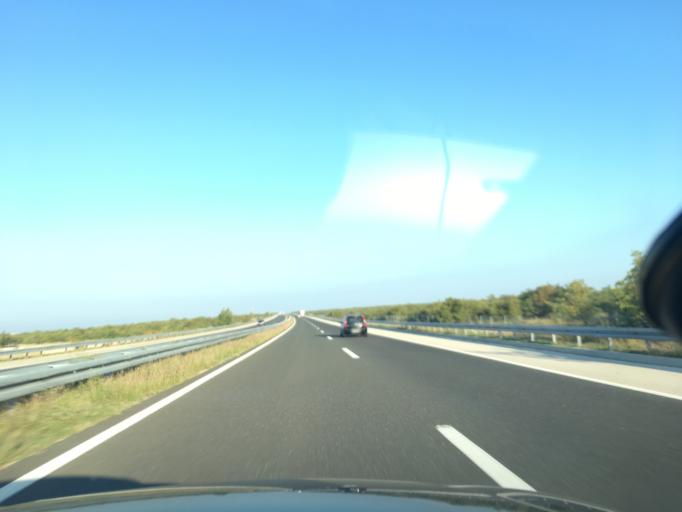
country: HR
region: Zadarska
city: Benkovac
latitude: 43.9931
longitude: 15.6191
